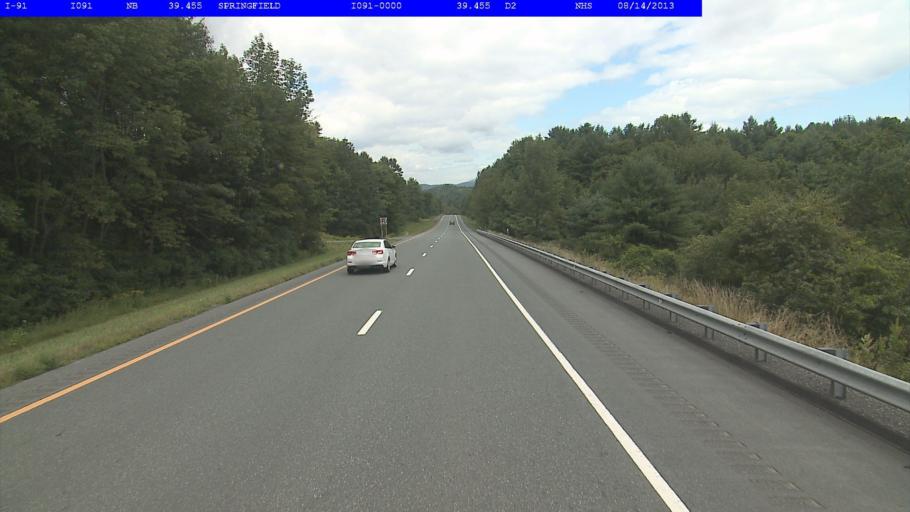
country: US
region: New Hampshire
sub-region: Sullivan County
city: Charlestown
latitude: 43.2372
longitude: -72.4474
